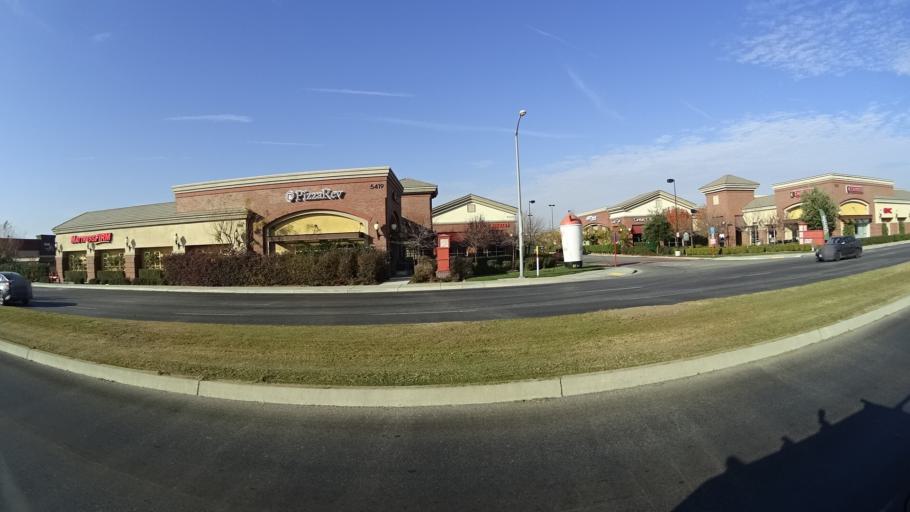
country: US
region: California
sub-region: Kern County
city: Greenacres
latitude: 35.3061
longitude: -119.0921
